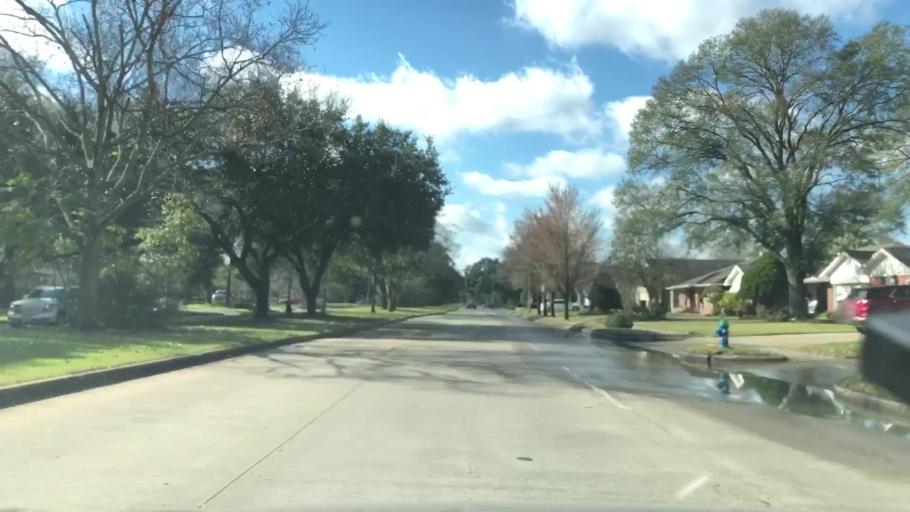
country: US
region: Texas
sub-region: Harris County
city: Bellaire
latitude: 29.6649
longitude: -95.4703
